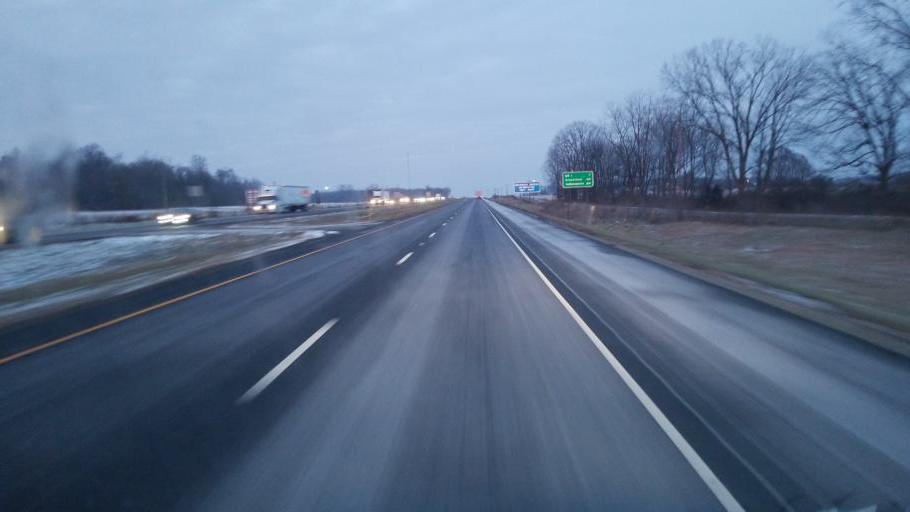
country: US
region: Indiana
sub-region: Wayne County
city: Centerville
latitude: 39.8596
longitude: -85.0061
